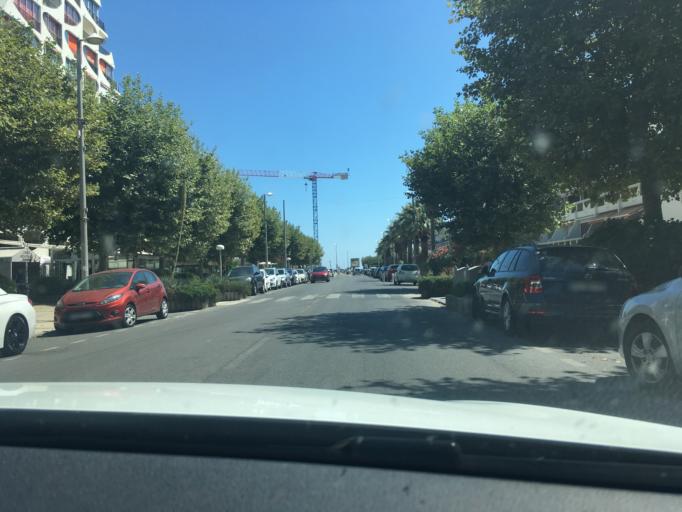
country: FR
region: Languedoc-Roussillon
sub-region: Departement de l'Herault
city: La Grande-Motte
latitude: 43.5591
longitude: 4.0854
